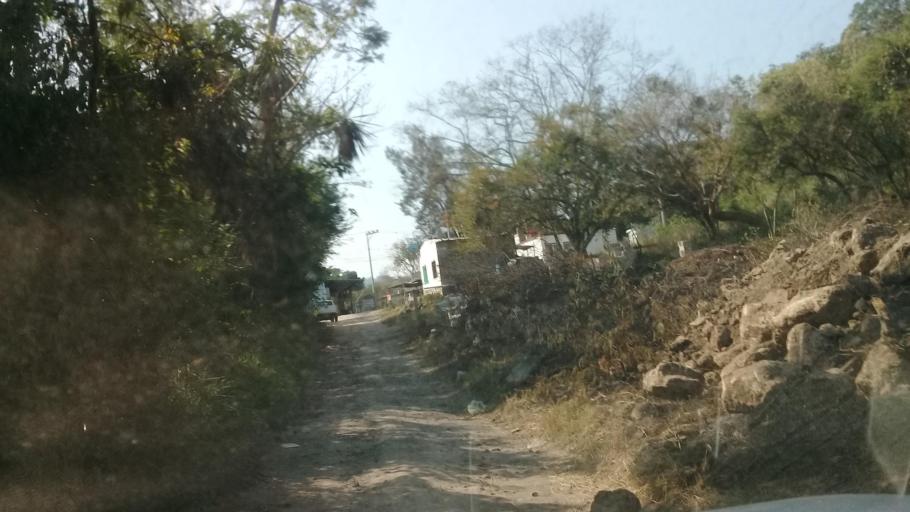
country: MX
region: Veracruz
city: El Castillo
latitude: 19.5717
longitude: -96.8360
